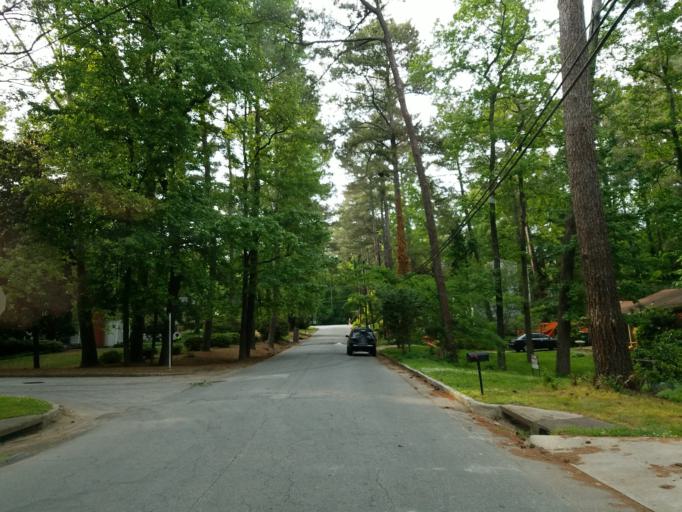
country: US
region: Georgia
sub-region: Cobb County
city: Vinings
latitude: 33.8232
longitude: -84.4461
